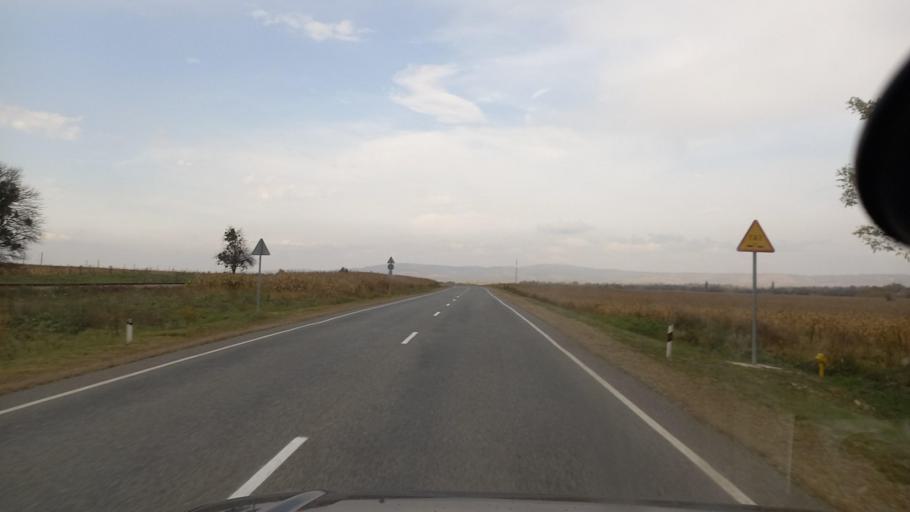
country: RU
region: Krasnodarskiy
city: Shedok
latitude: 44.2526
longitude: 40.8653
